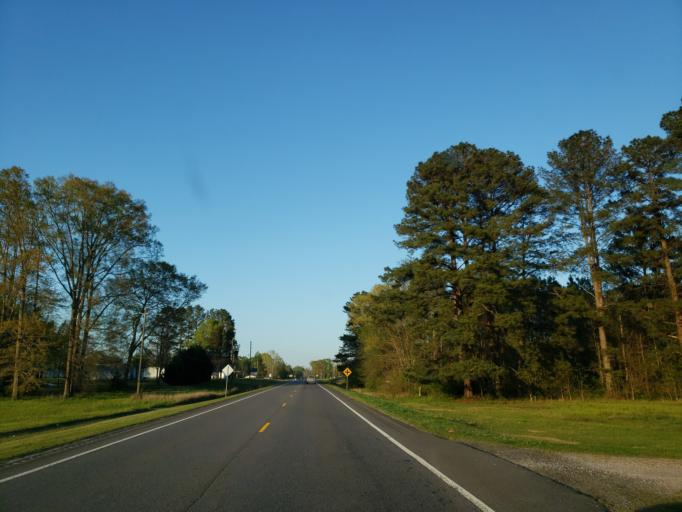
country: US
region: Alabama
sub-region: Sumter County
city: York
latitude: 32.4351
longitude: -88.3727
